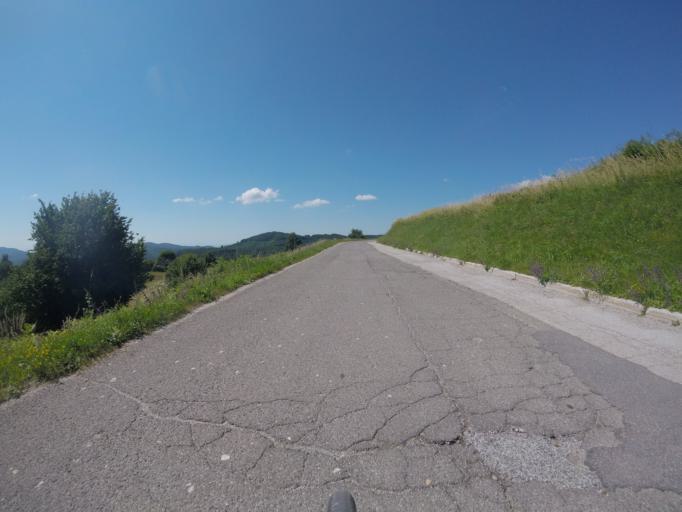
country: SI
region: Kostanjevica na Krki
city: Kostanjevica na Krki
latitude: 45.8111
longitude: 15.5109
